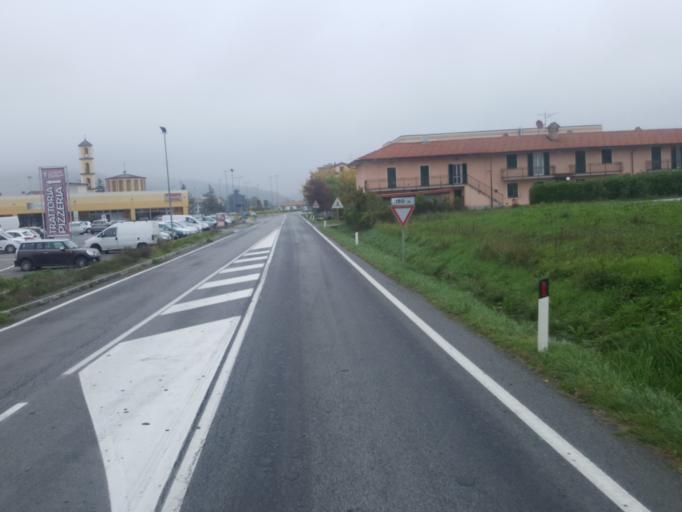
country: IT
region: Piedmont
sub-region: Provincia di Cuneo
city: Ceva
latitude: 44.3755
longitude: 8.0407
